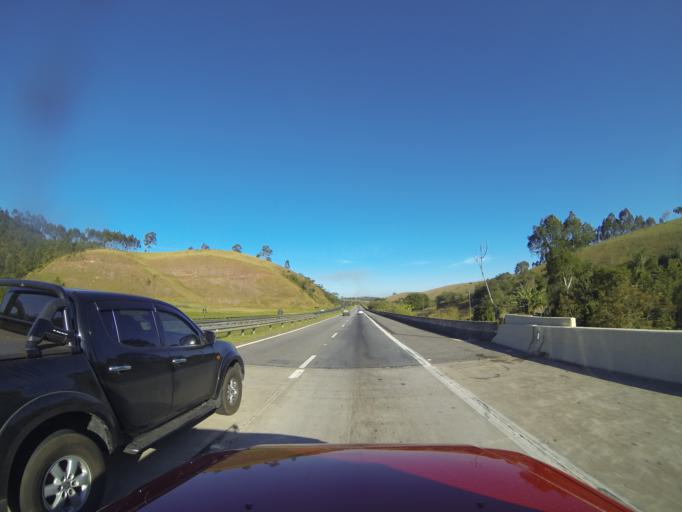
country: BR
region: Sao Paulo
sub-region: Santa Isabel
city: Santa Isabel
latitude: -23.1774
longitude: -46.2103
